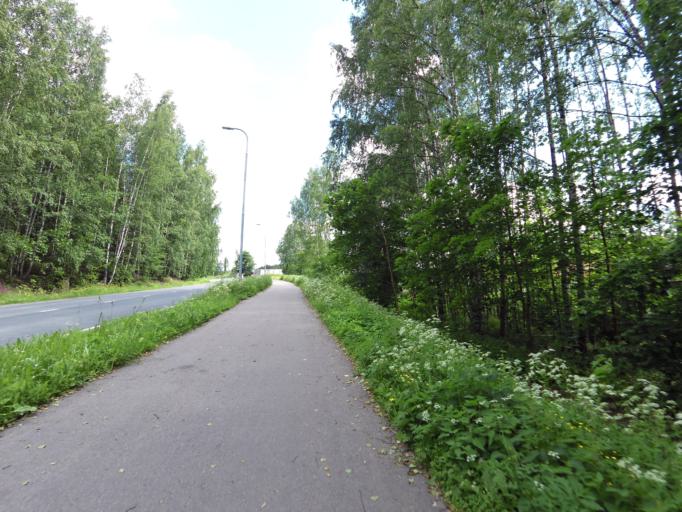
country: FI
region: Pirkanmaa
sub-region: Tampere
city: Pirkkala
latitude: 61.5037
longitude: 23.6383
